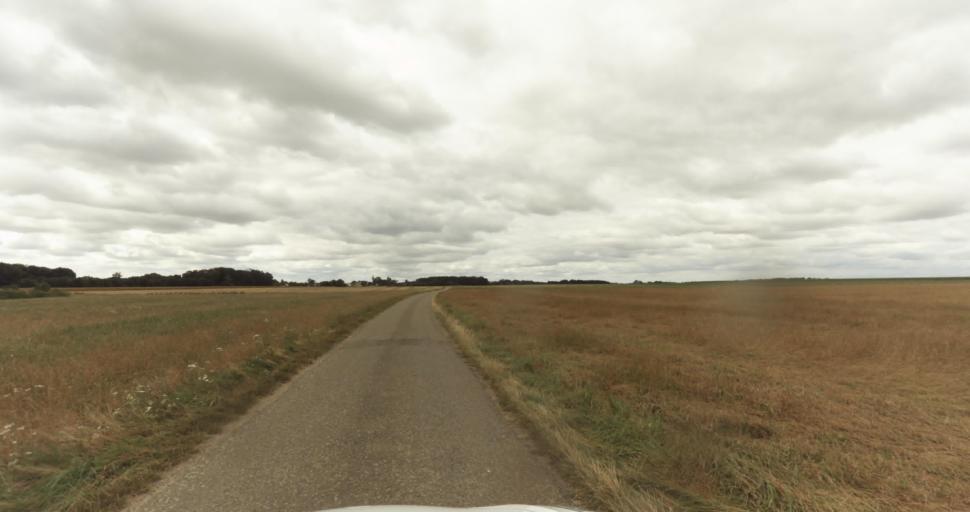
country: FR
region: Haute-Normandie
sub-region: Departement de l'Eure
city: Nonancourt
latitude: 48.8062
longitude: 1.1683
